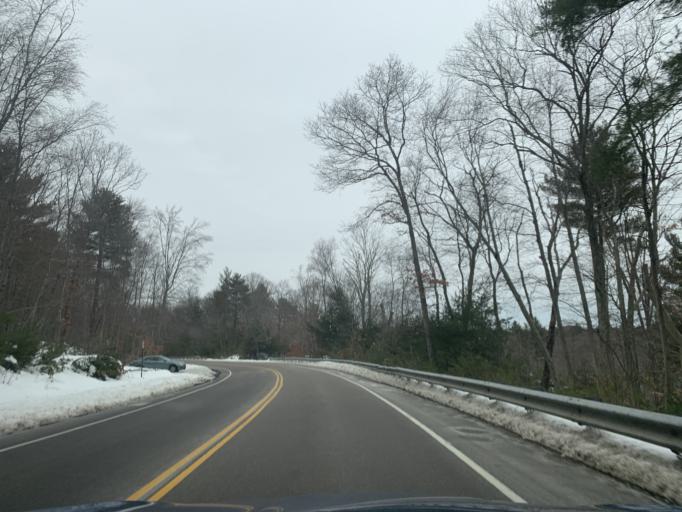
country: US
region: Massachusetts
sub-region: Norfolk County
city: Milton
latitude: 42.2202
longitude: -71.0906
